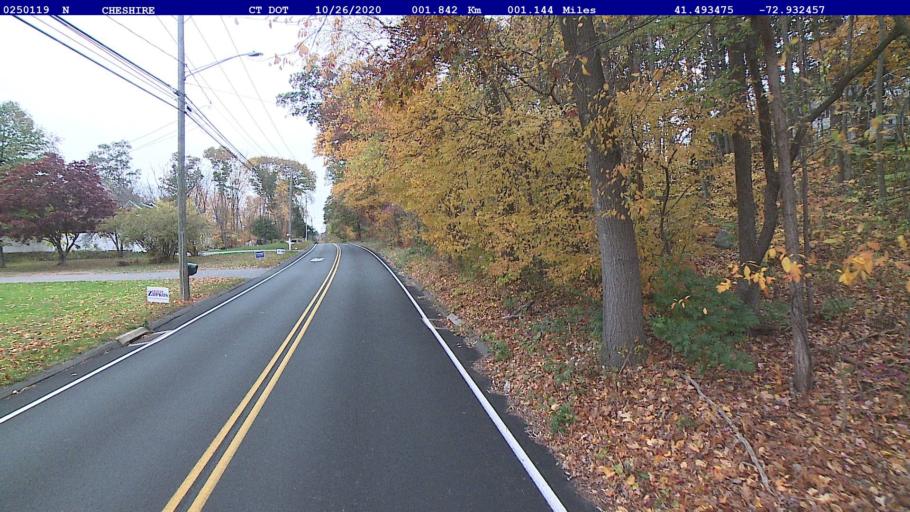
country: US
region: Connecticut
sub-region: New Haven County
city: Cheshire
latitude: 41.4935
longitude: -72.9324
